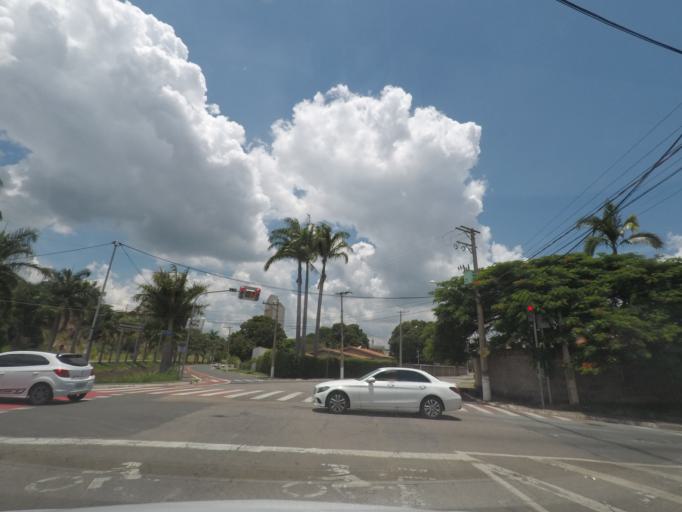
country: BR
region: Sao Paulo
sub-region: Vinhedo
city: Vinhedo
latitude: -23.0225
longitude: -46.9809
